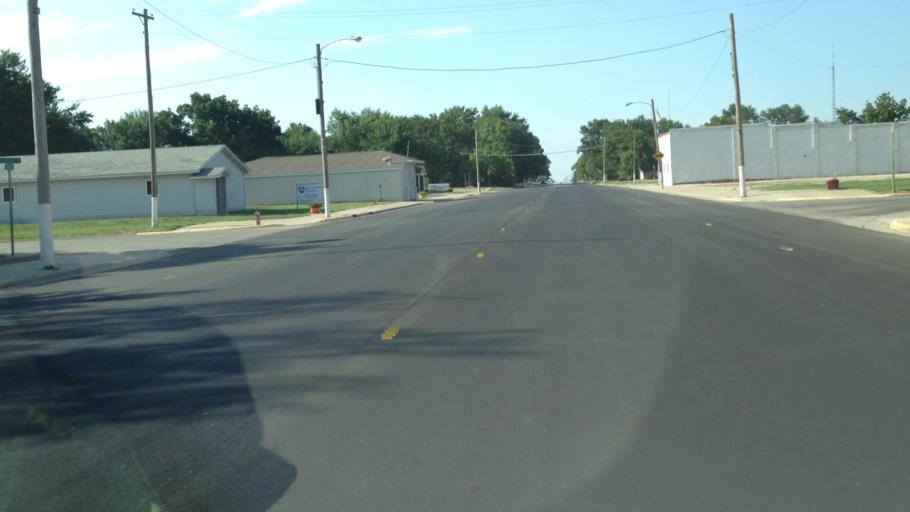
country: US
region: Kansas
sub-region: Allen County
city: Iola
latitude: 37.9153
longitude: -95.1701
